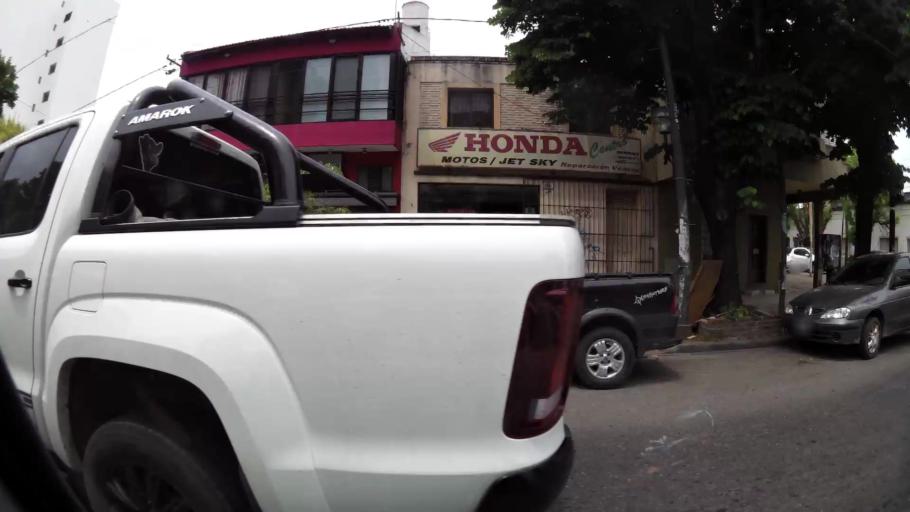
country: AR
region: Buenos Aires
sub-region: Partido de La Plata
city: La Plata
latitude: -34.9256
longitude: -57.9715
